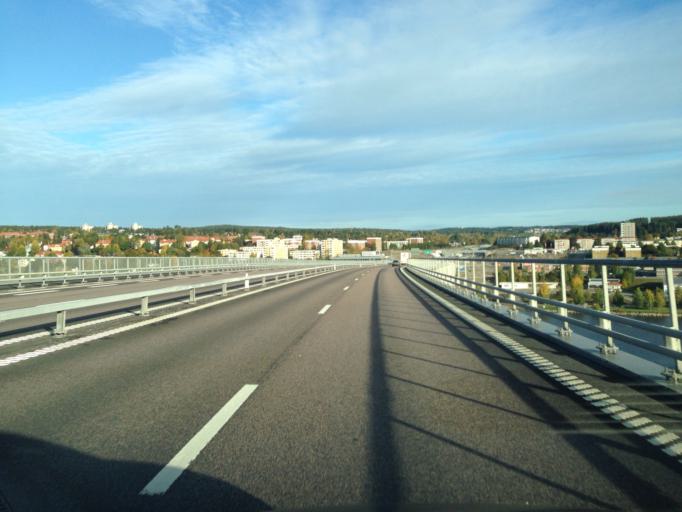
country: SE
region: Vaesternorrland
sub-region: Sundsvalls Kommun
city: Sundsvall
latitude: 62.3906
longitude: 17.3397
